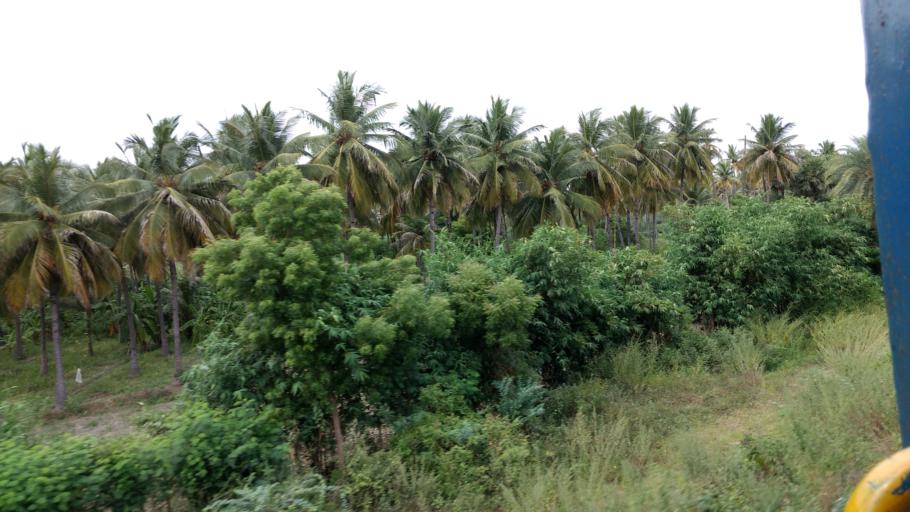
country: IN
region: Tamil Nadu
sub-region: Vellore
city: Gudiyatham
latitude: 12.9218
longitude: 78.8813
